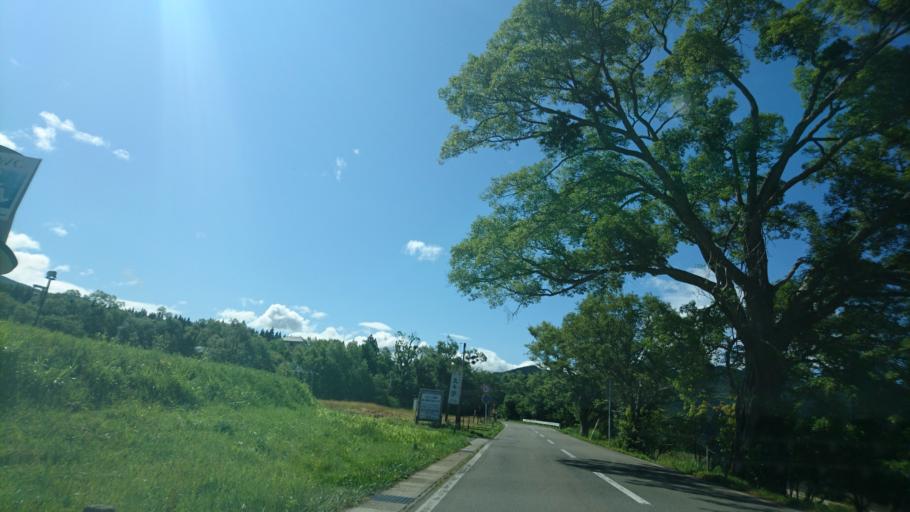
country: JP
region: Akita
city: Kakunodatemachi
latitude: 39.7378
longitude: 140.6940
